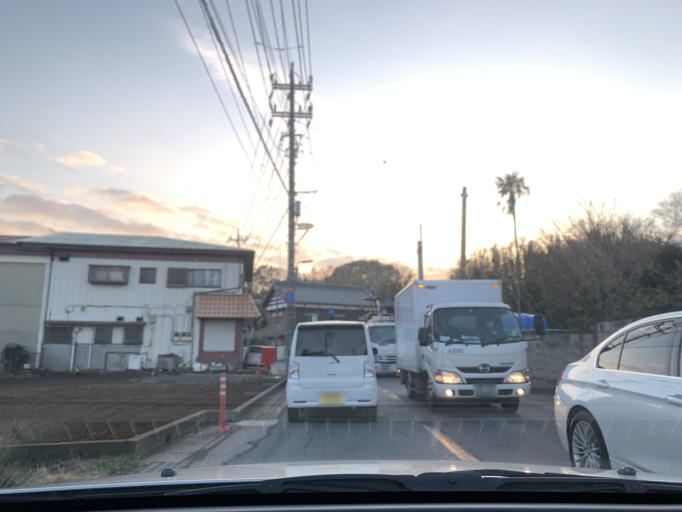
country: JP
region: Chiba
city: Matsudo
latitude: 35.7627
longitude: 139.9193
